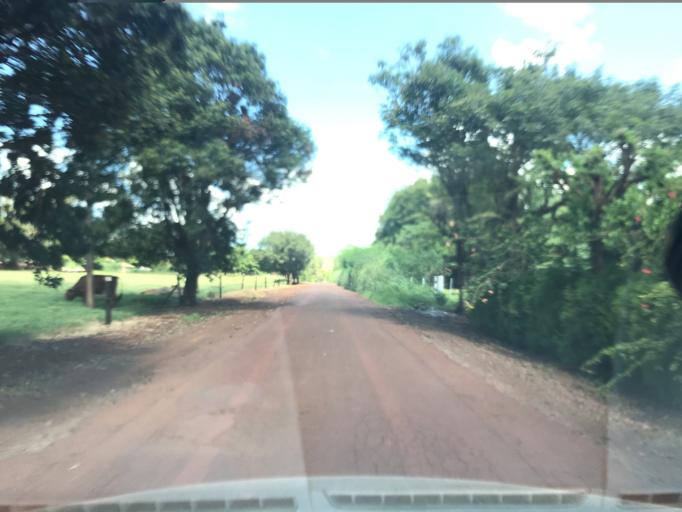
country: BR
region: Parana
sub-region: Palotina
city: Palotina
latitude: -24.2953
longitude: -53.8594
